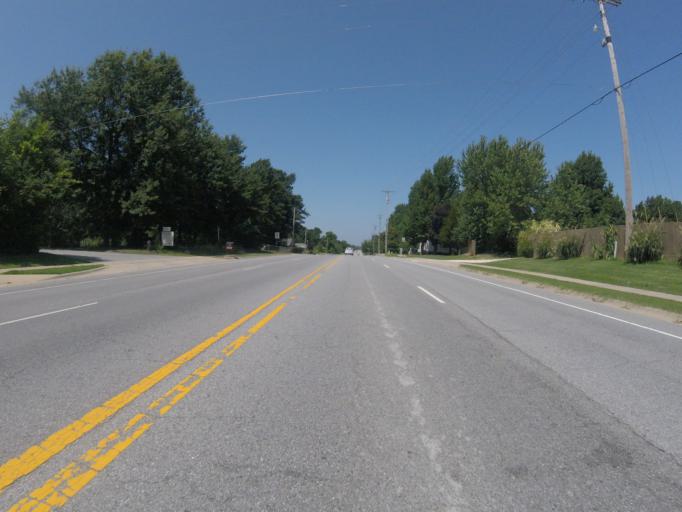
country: US
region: Arkansas
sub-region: Washington County
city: Fayetteville
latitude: 36.0926
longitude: -94.1948
